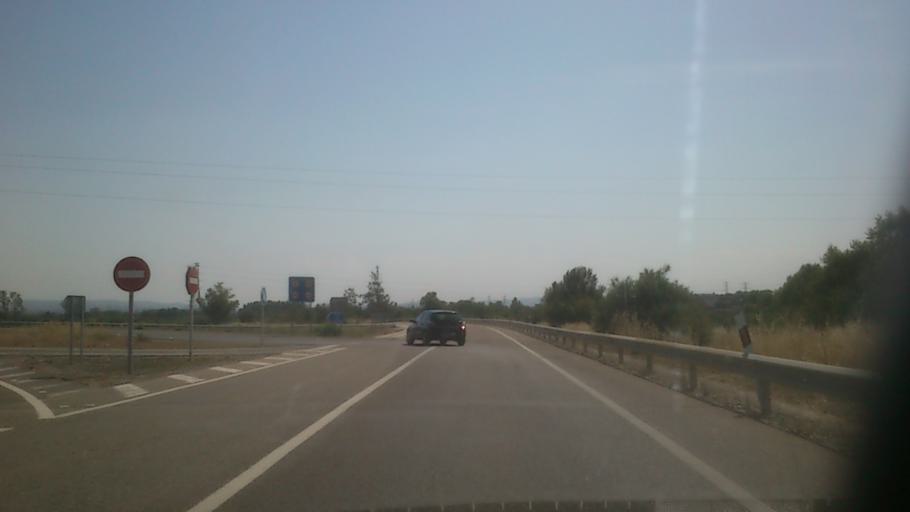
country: ES
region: Aragon
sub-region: Provincia de Zaragoza
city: Zaragoza
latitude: 41.6933
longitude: -0.8366
